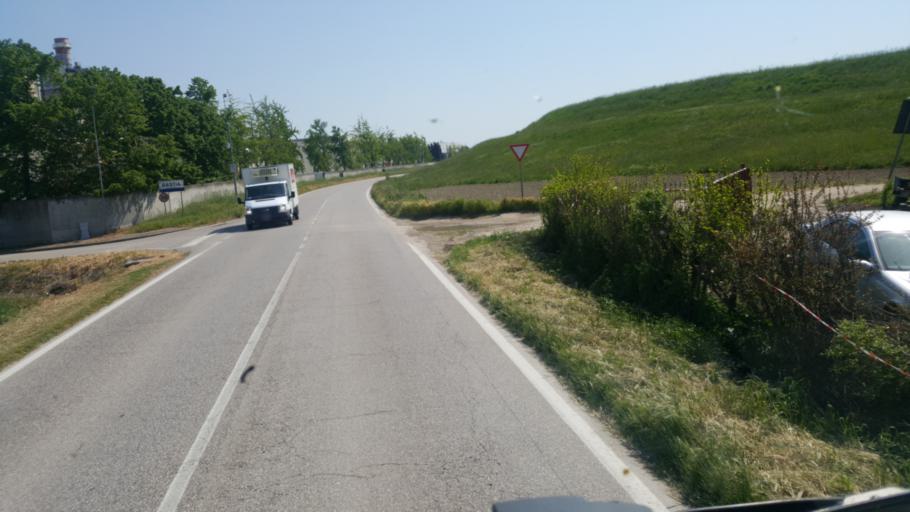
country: IT
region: Lombardy
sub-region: Provincia di Mantova
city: Sustinente
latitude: 45.0685
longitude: 11.0419
